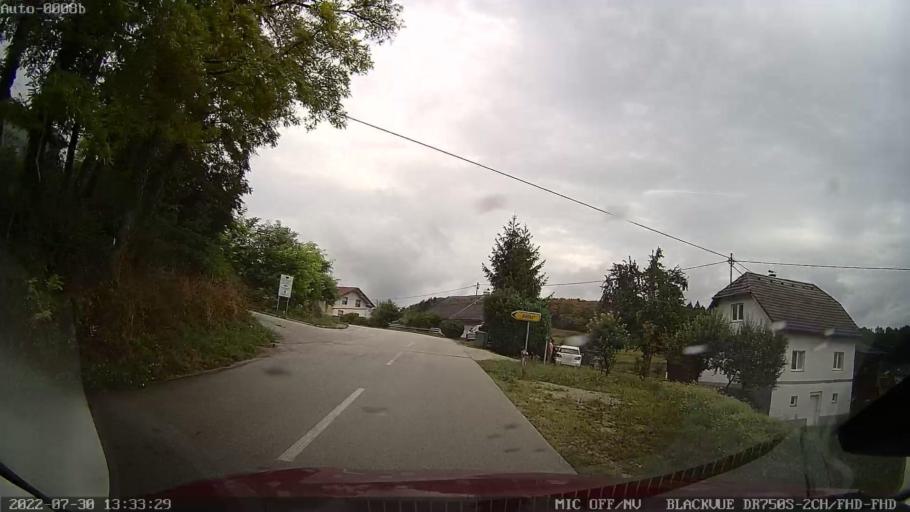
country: SI
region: Zuzemberk
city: Zuzemberk
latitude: 45.8519
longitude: 14.9356
